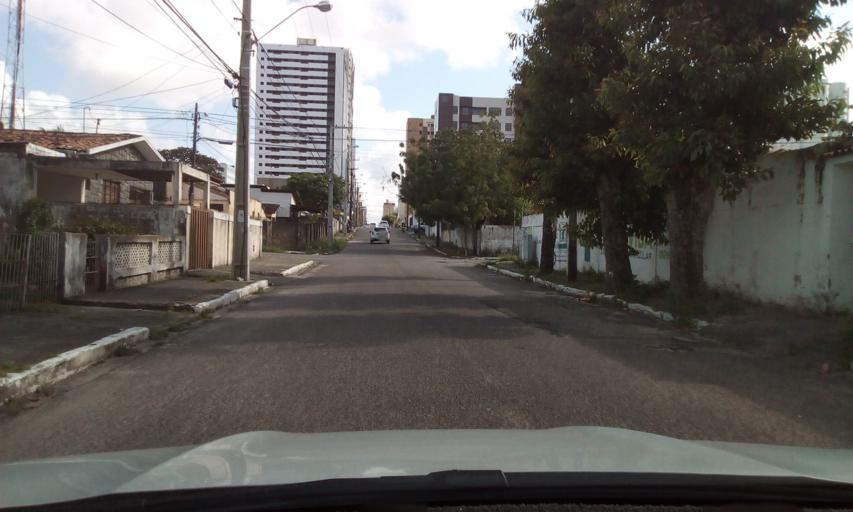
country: BR
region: Paraiba
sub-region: Joao Pessoa
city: Joao Pessoa
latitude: -7.1243
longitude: -34.8533
